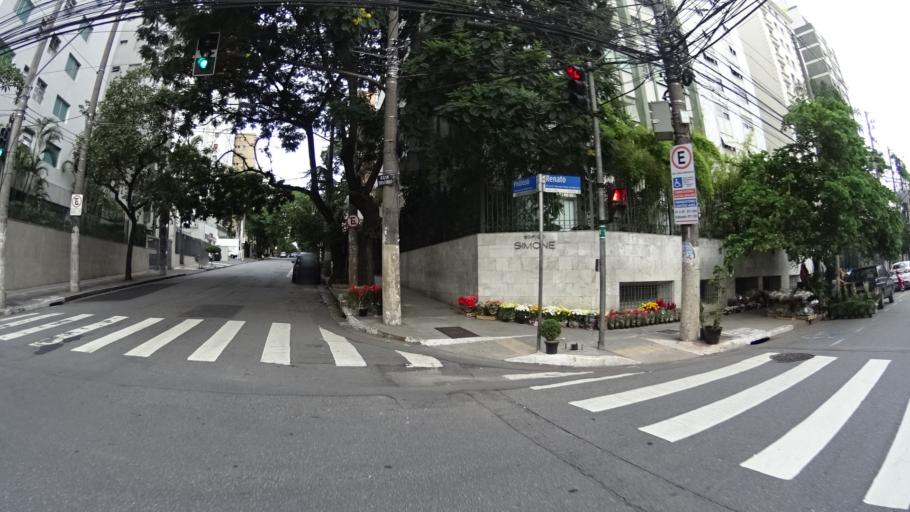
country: BR
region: Sao Paulo
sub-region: Sao Paulo
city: Sao Paulo
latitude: -23.5809
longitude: -46.6750
